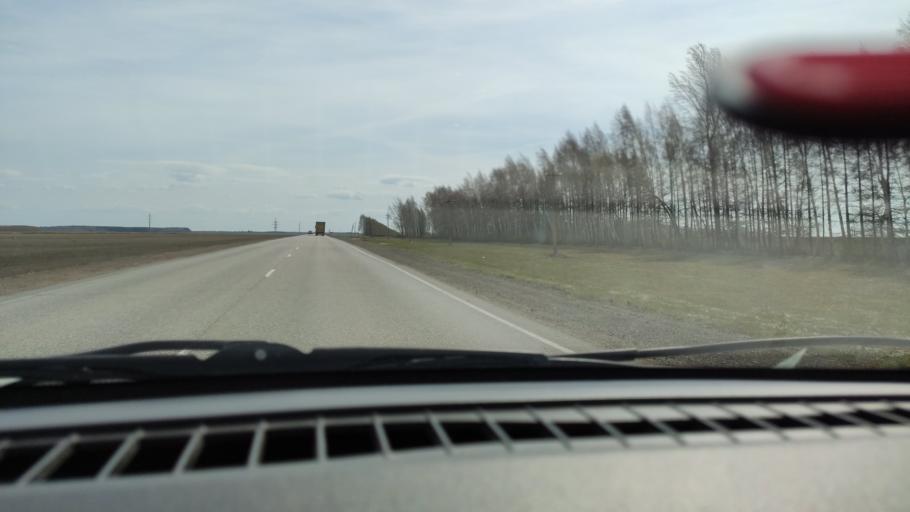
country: RU
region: Bashkortostan
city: Dyurtyuli
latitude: 55.3376
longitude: 54.9488
